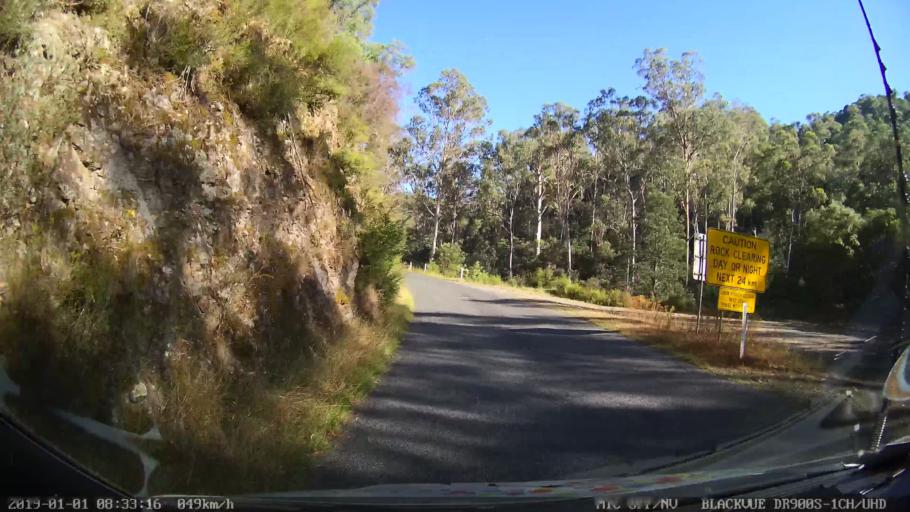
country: AU
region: New South Wales
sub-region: Snowy River
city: Jindabyne
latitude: -36.3560
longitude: 148.2031
